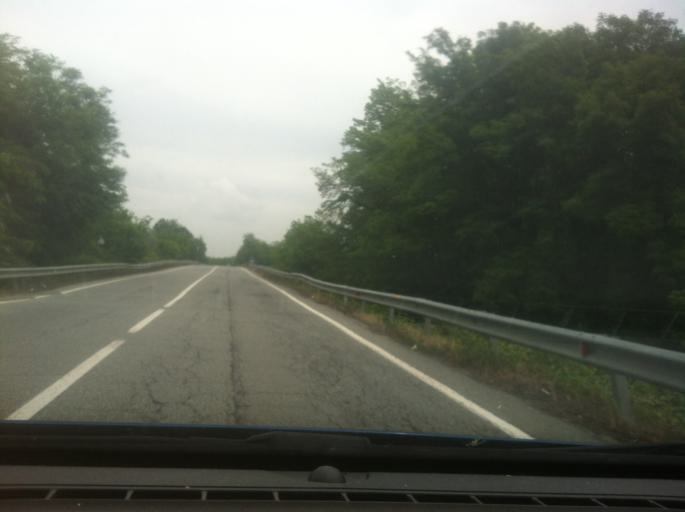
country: IT
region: Piedmont
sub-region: Provincia di Torino
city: San Benigno Canavese
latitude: 45.2458
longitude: 7.8043
